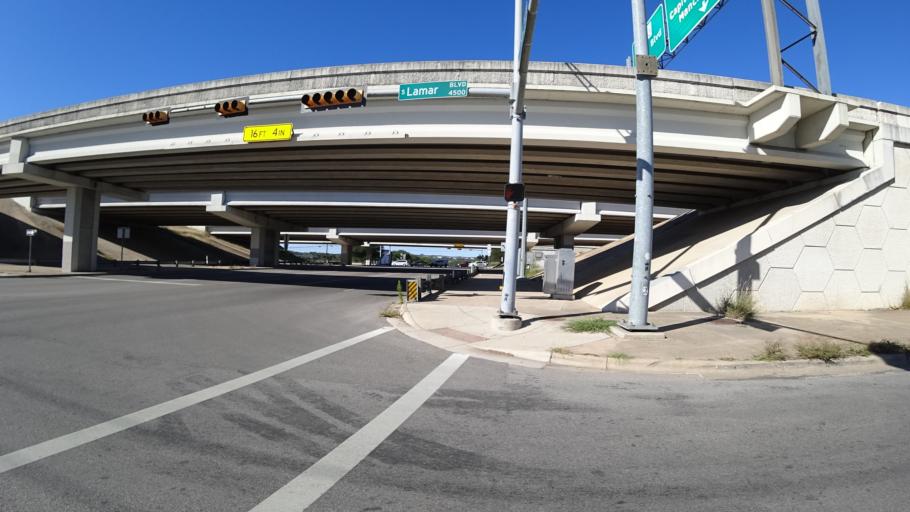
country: US
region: Texas
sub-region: Travis County
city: Rollingwood
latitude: 30.2320
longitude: -97.8004
